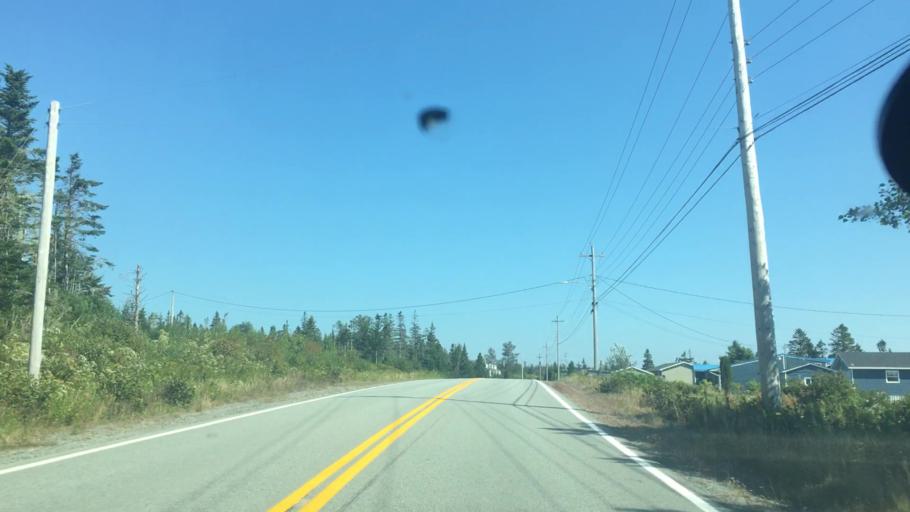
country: CA
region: Nova Scotia
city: New Glasgow
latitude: 44.9284
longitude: -62.2978
